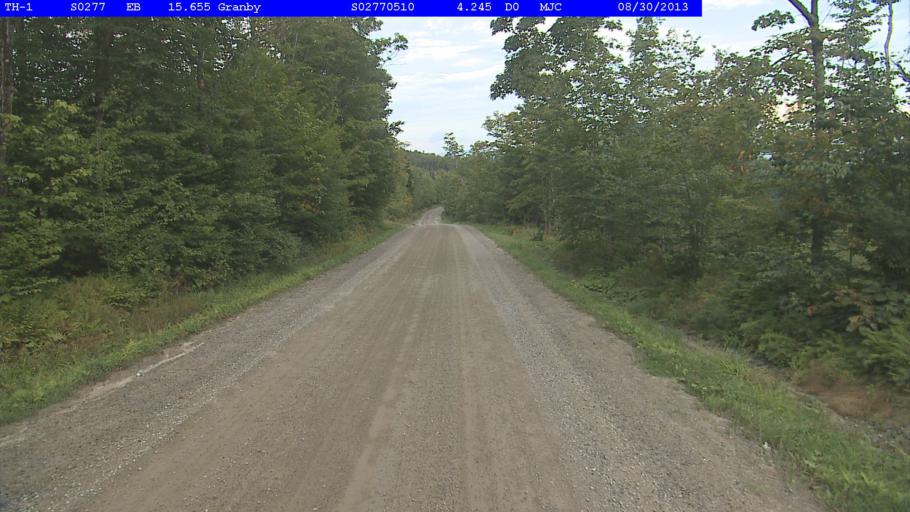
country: US
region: Vermont
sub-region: Essex County
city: Guildhall
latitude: 44.5769
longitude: -71.6880
